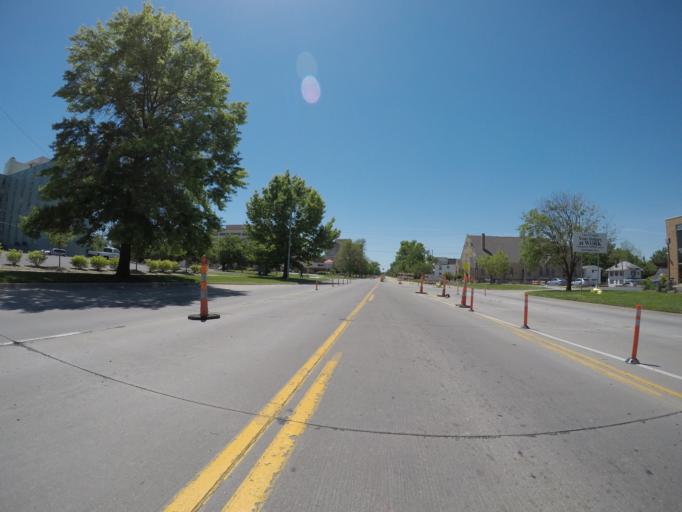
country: US
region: Kansas
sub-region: Shawnee County
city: Topeka
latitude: 39.0523
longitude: -95.6794
